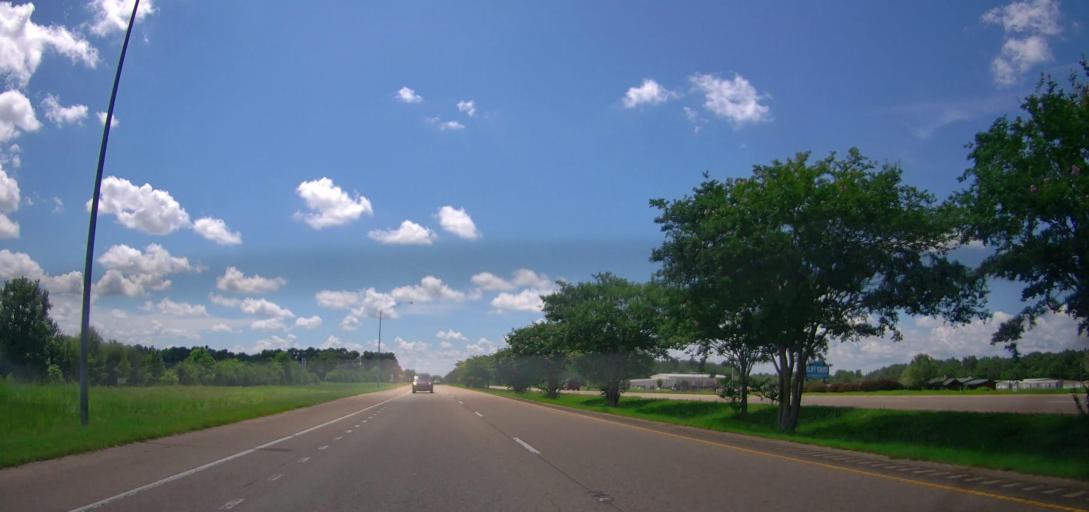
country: US
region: Alabama
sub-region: Elmore County
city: Blue Ridge
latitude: 32.4217
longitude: -86.2343
